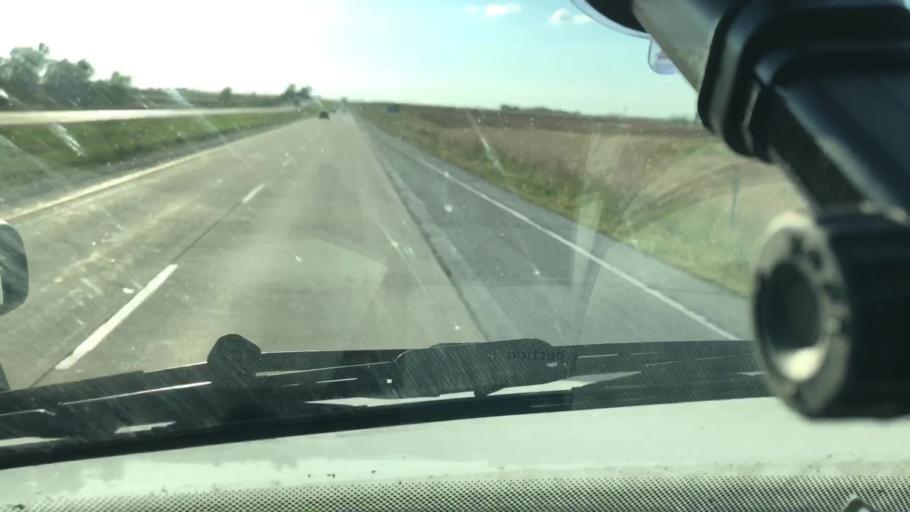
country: US
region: Iowa
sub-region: Pottawattamie County
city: Avoca
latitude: 41.4993
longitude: -95.4974
